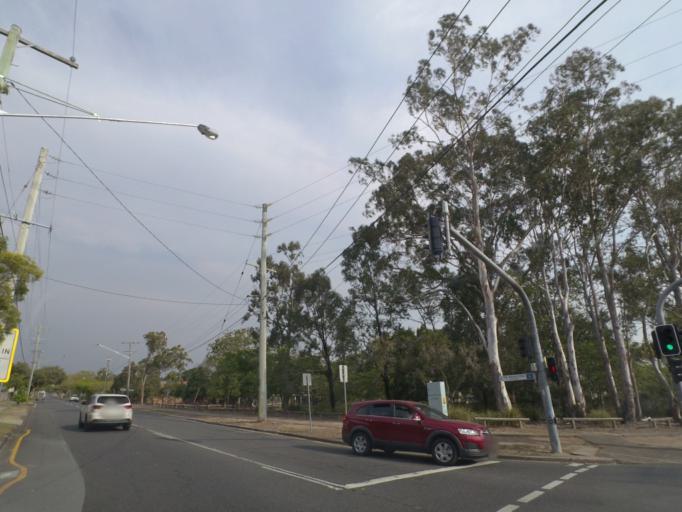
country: AU
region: Queensland
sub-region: Brisbane
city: Robertson
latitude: -27.5646
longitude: 153.0497
